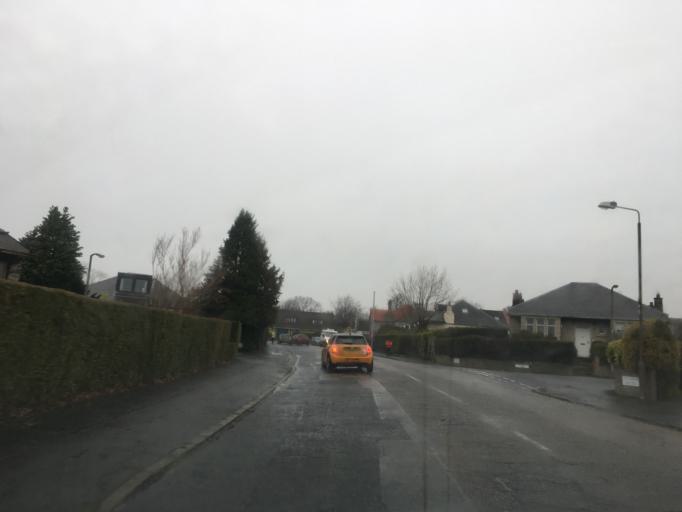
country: GB
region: Scotland
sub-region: Edinburgh
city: Colinton
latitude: 55.9472
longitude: -3.2893
